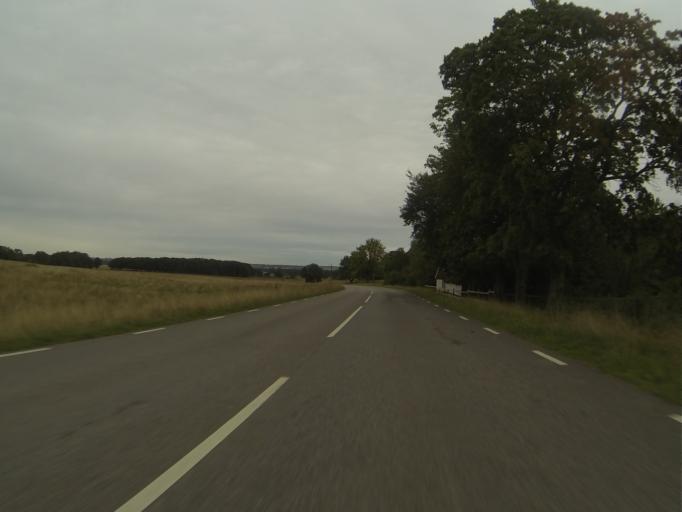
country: SE
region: Skane
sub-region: Lunds Kommun
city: Veberod
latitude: 55.6958
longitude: 13.4220
